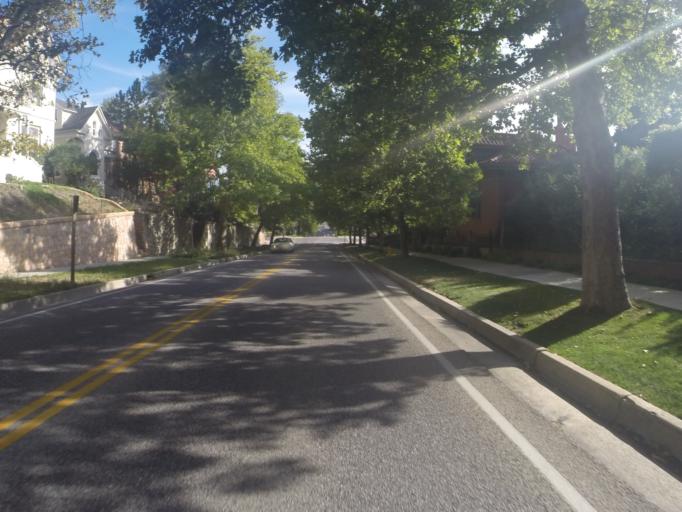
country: US
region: Utah
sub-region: Salt Lake County
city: Salt Lake City
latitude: 40.7744
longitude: -111.8883
